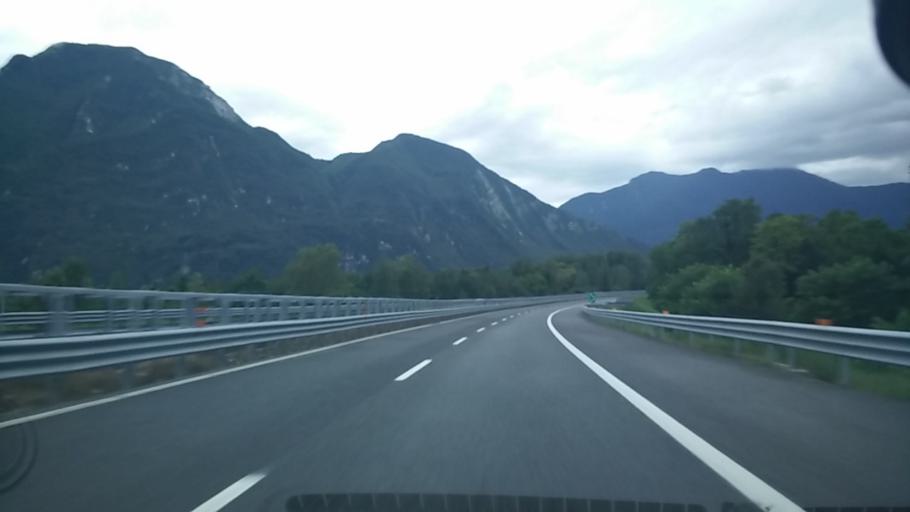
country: IT
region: Friuli Venezia Giulia
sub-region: Provincia di Udine
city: Amaro
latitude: 46.3793
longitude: 13.1166
